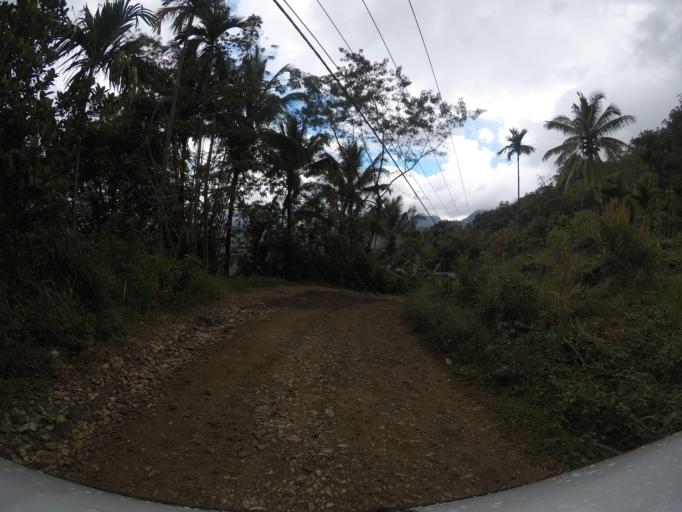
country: TL
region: Baucau
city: Baucau
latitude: -8.6400
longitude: 126.6394
